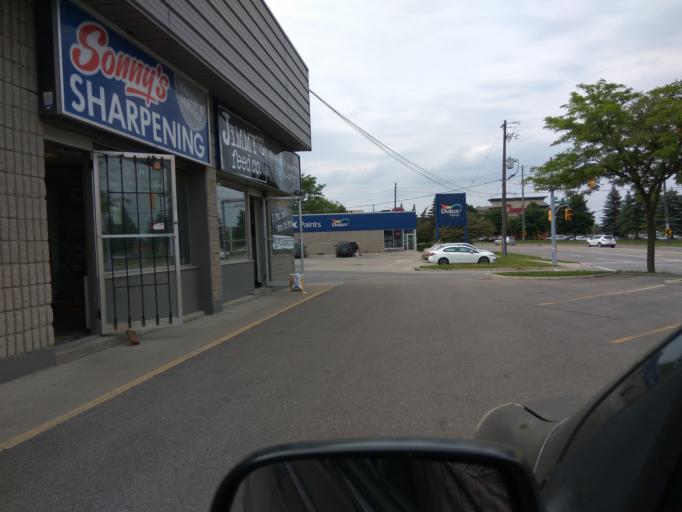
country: CA
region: Ontario
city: Waterloo
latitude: 43.4843
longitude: -80.5254
